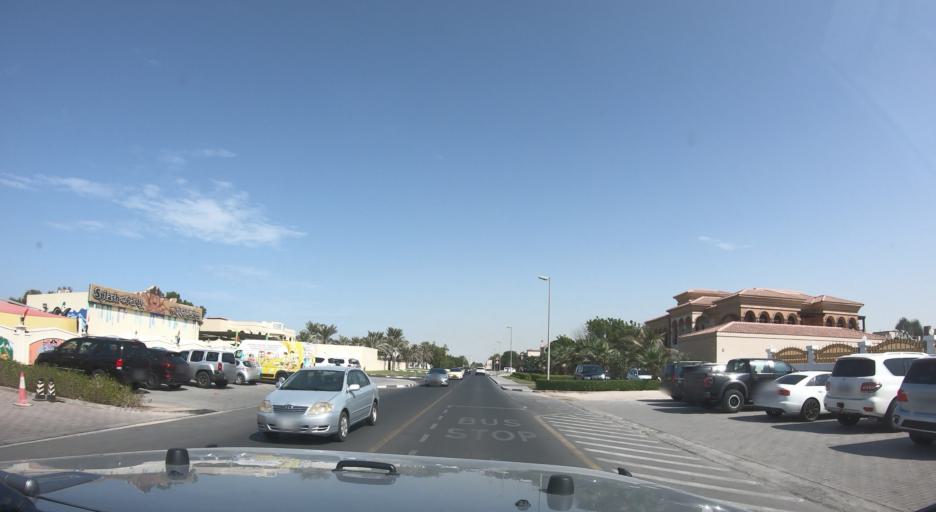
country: AE
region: Dubai
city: Dubai
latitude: 25.1593
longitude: 55.2237
